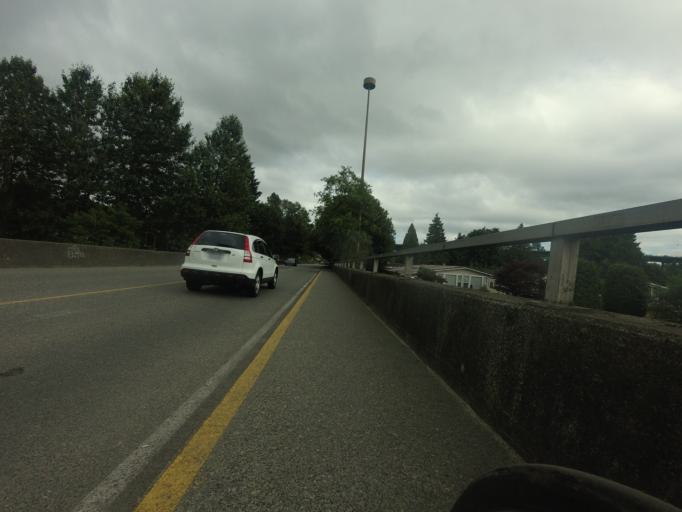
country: CA
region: British Columbia
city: West End
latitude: 49.3244
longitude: -123.1331
